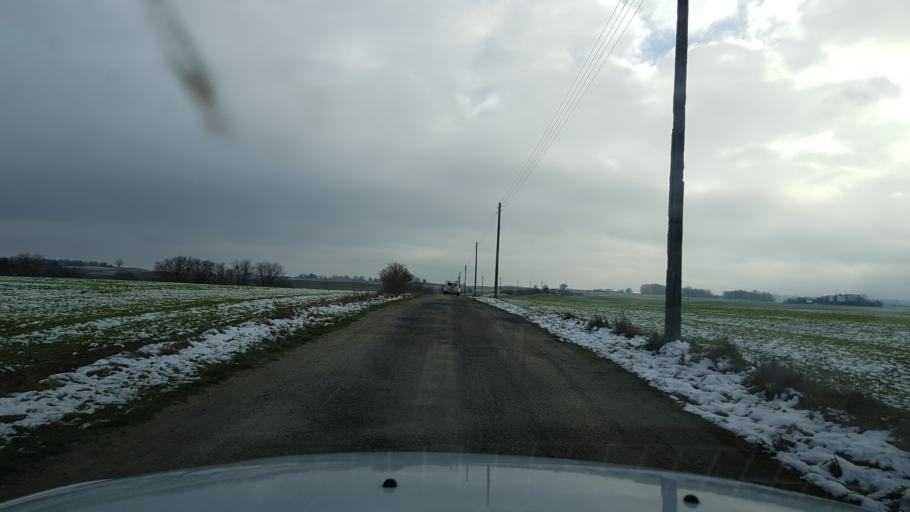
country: PL
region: West Pomeranian Voivodeship
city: Trzcinsko Zdroj
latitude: 52.9584
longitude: 14.6821
